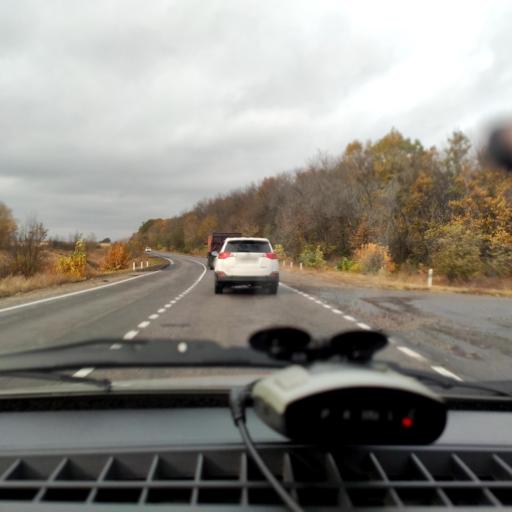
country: RU
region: Voronezj
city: Kolodeznyy
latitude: 51.3784
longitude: 39.0187
